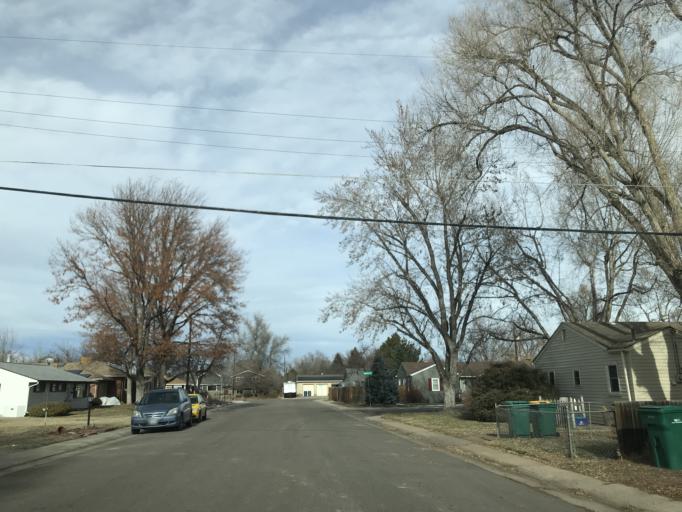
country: US
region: Colorado
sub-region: Arapahoe County
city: Littleton
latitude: 39.6032
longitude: -105.0140
